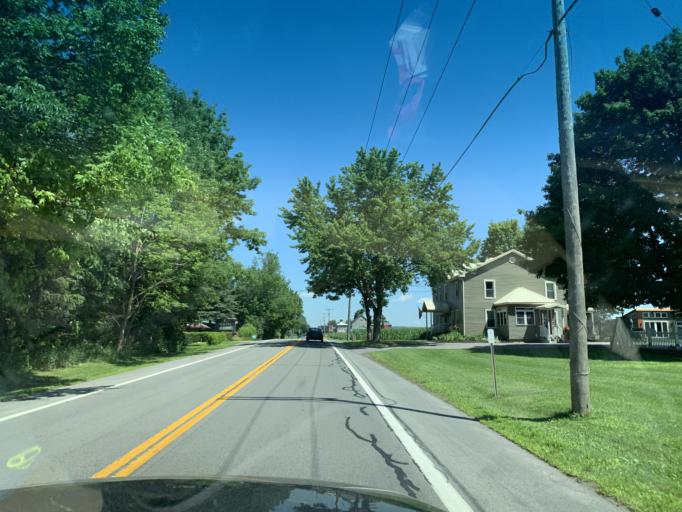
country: US
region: New York
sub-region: Oneida County
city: Chadwicks
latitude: 42.8916
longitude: -75.2465
